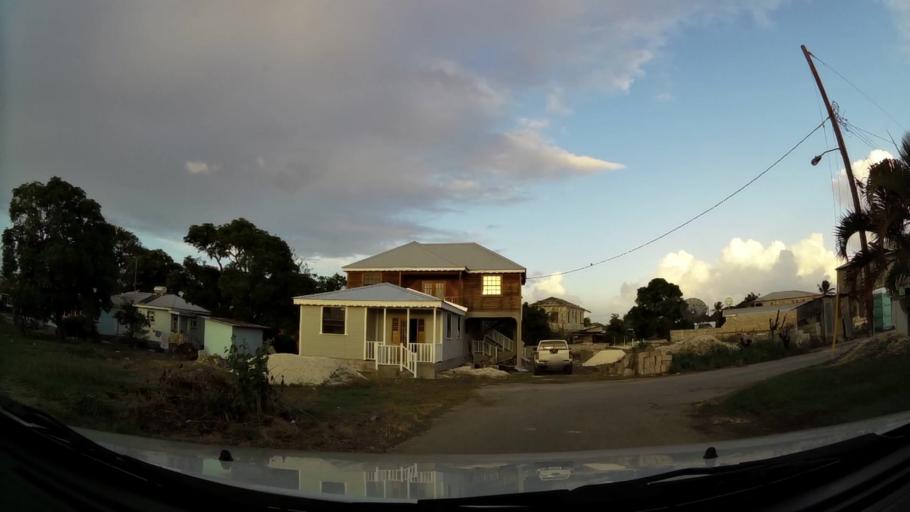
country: BB
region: Saint Philip
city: Crane
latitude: 13.1036
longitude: -59.4694
